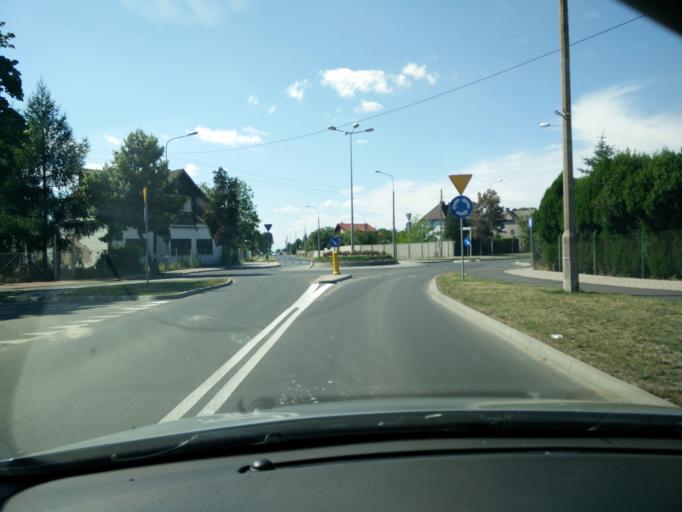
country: PL
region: Greater Poland Voivodeship
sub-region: Powiat sredzki
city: Sroda Wielkopolska
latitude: 52.2273
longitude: 17.2660
